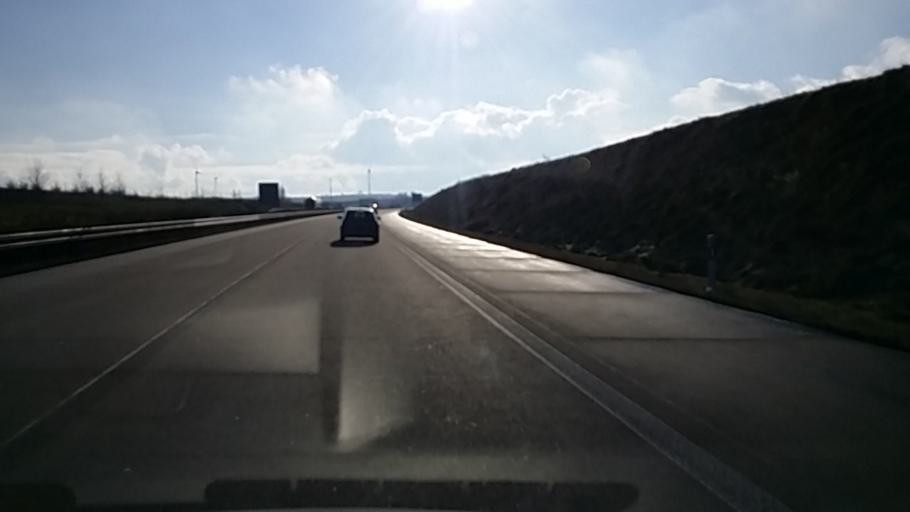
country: DE
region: Saxony
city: Liebstadt
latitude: 50.8275
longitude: 13.8872
